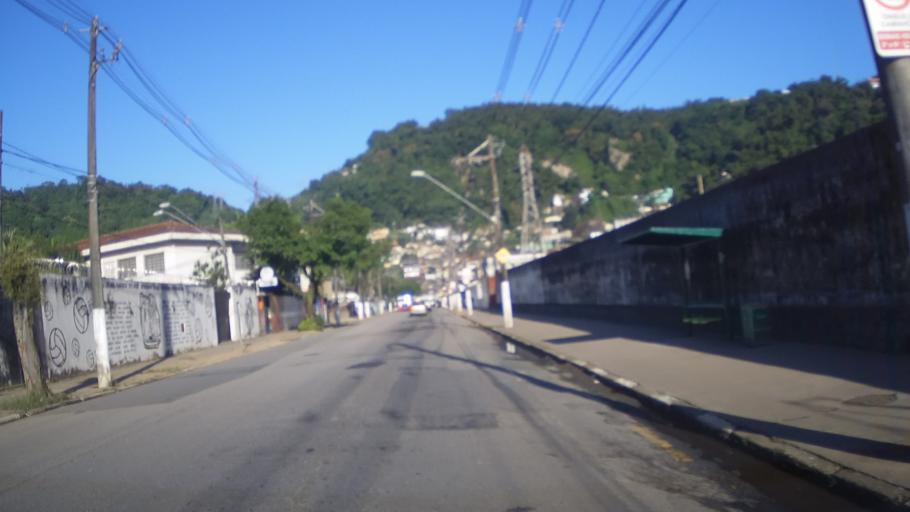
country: BR
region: Sao Paulo
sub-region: Santos
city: Santos
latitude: -23.9420
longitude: -46.3384
